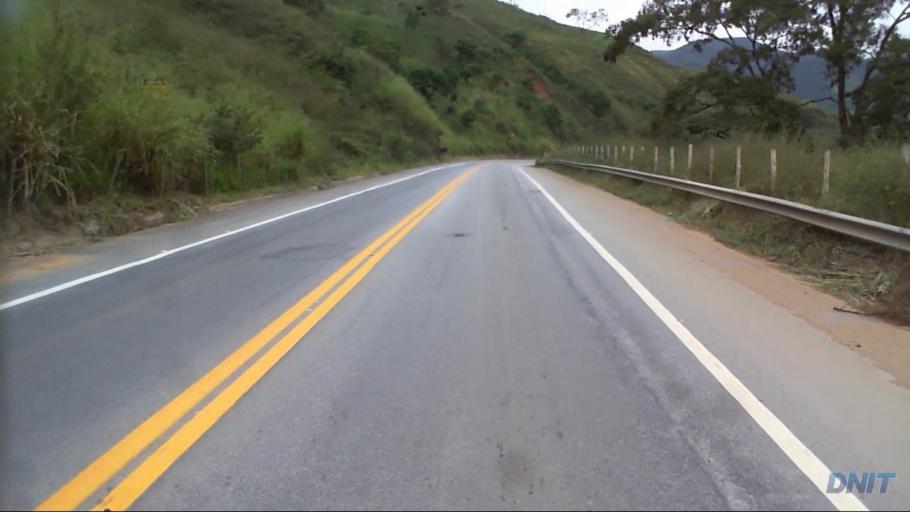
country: BR
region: Minas Gerais
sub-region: Timoteo
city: Timoteo
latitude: -19.6191
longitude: -42.7777
